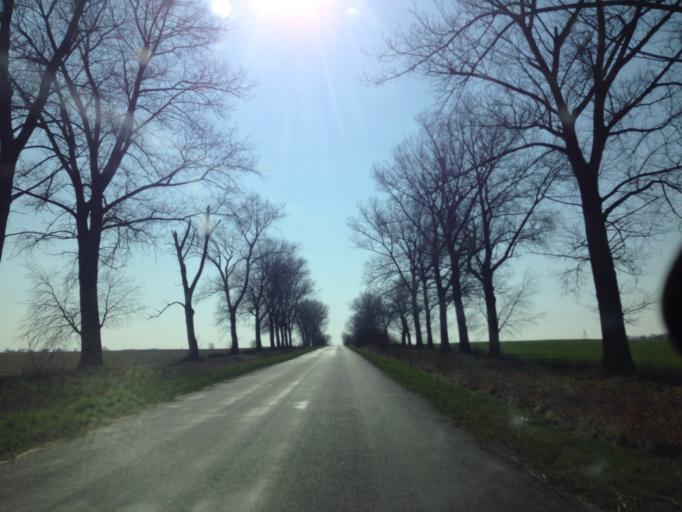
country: PL
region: Lower Silesian Voivodeship
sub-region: Powiat olesnicki
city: Bierutow
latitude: 51.2024
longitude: 17.6100
